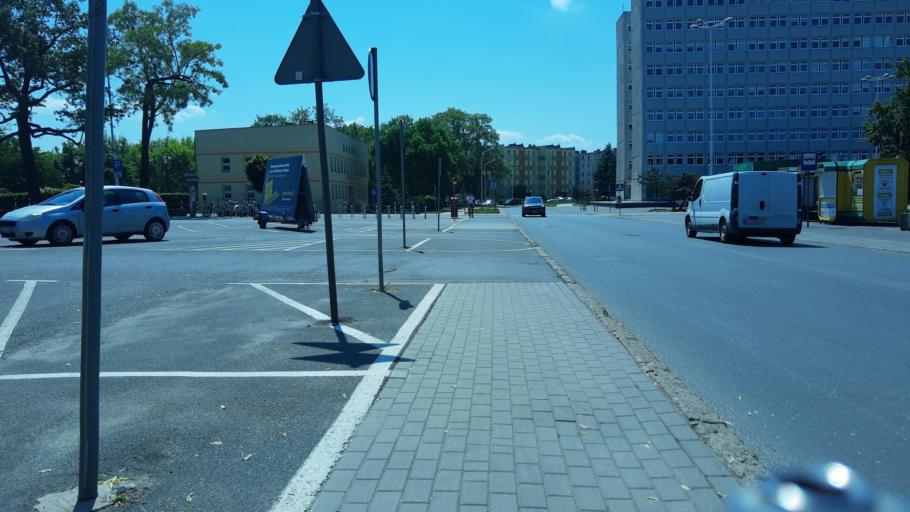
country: PL
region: Lodz Voivodeship
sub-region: Powiat sieradzki
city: Sieradz
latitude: 51.5942
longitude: 18.7344
